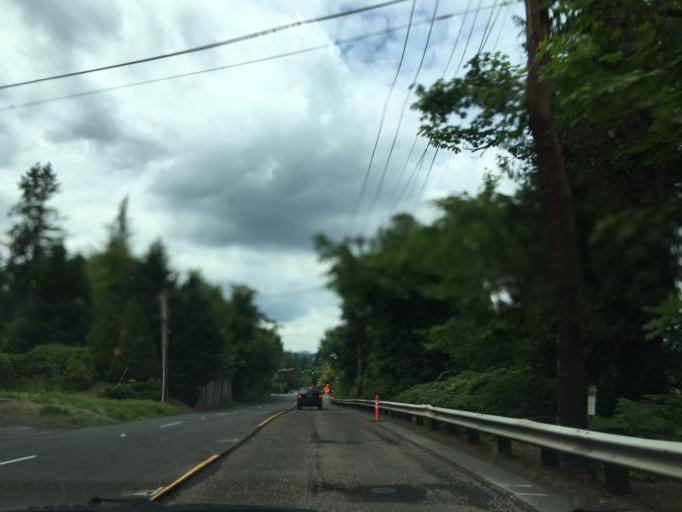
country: US
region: Oregon
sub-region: Clackamas County
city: Milwaukie
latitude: 45.4492
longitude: -122.6583
